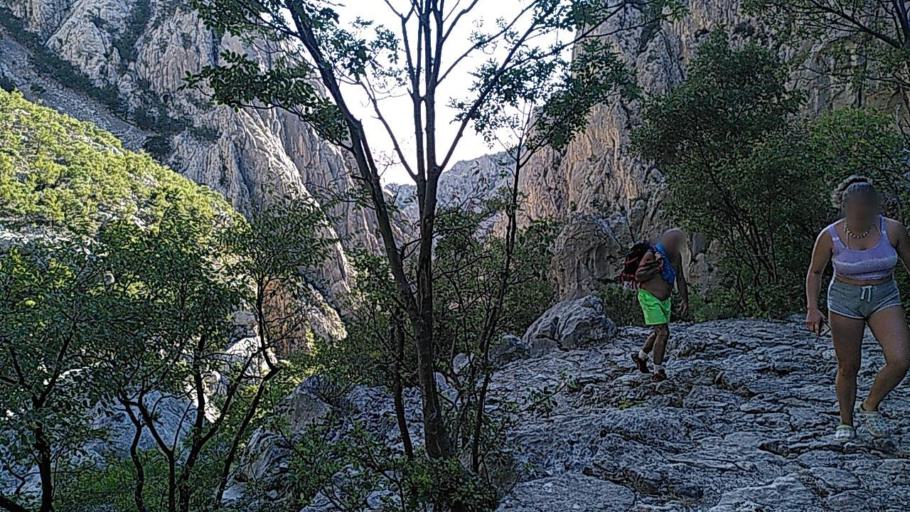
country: HR
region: Zadarska
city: Starigrad
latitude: 44.3087
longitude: 15.4778
